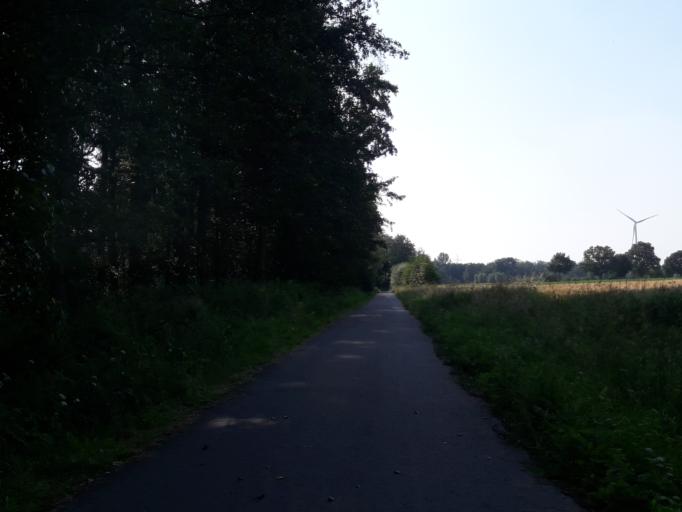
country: DE
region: North Rhine-Westphalia
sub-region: Regierungsbezirk Detmold
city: Salzkotten
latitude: 51.6828
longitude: 8.6710
